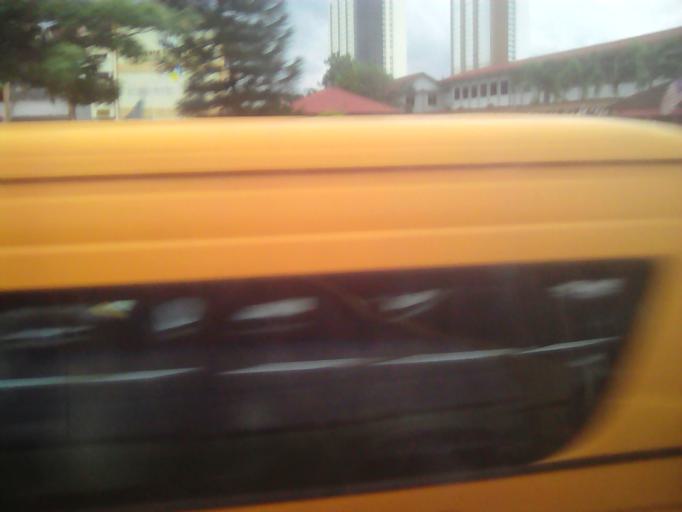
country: MY
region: Penang
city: Butterworth
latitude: 5.4007
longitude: 100.3744
